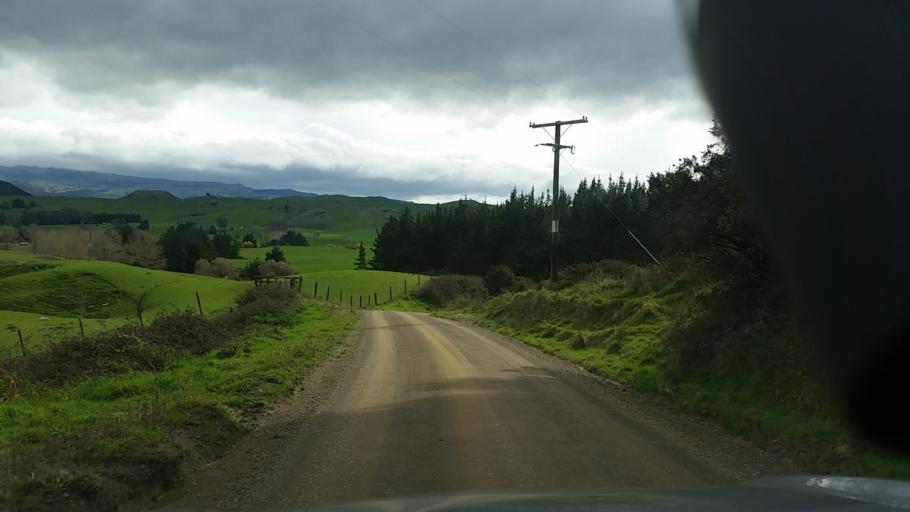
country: NZ
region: Hawke's Bay
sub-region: Napier City
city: Napier
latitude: -39.1903
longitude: 176.9142
